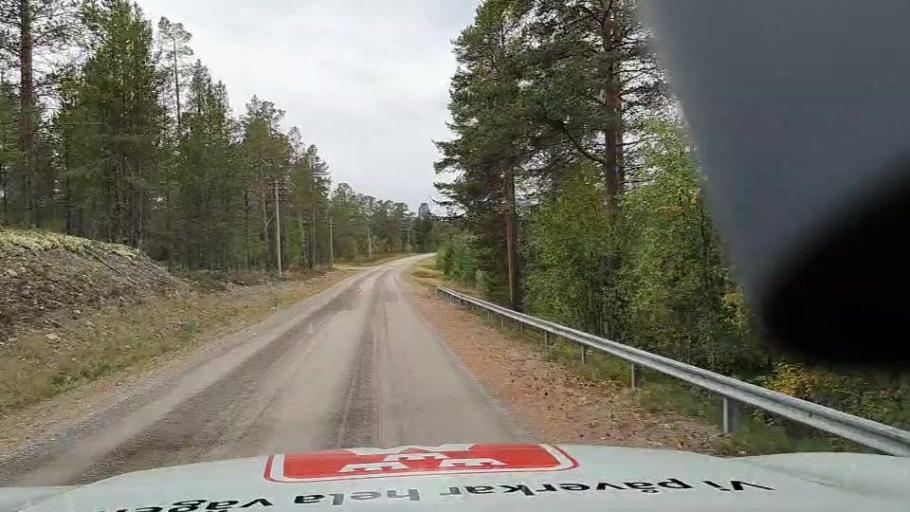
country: NO
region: Hedmark
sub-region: Engerdal
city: Engerdal
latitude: 62.0517
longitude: 12.7257
